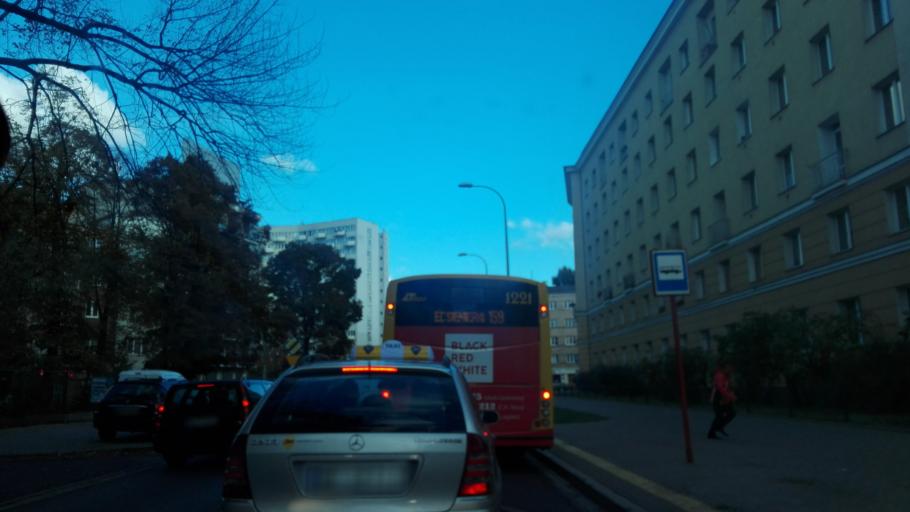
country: PL
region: Masovian Voivodeship
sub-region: Warszawa
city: Ochota
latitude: 52.2213
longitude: 20.9837
